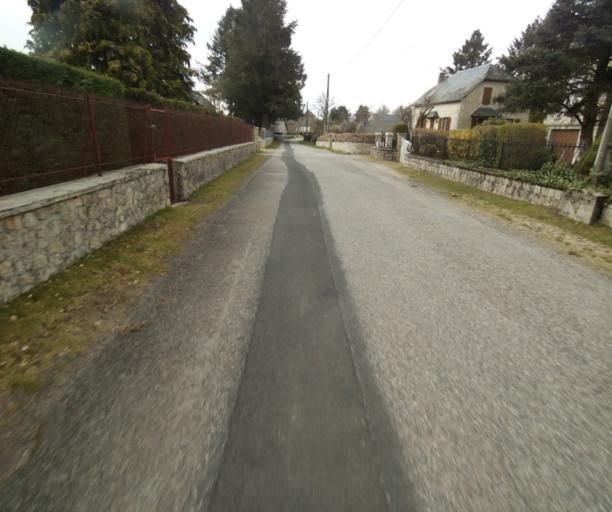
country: FR
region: Limousin
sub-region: Departement de la Correze
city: Correze
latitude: 45.2822
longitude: 1.9725
